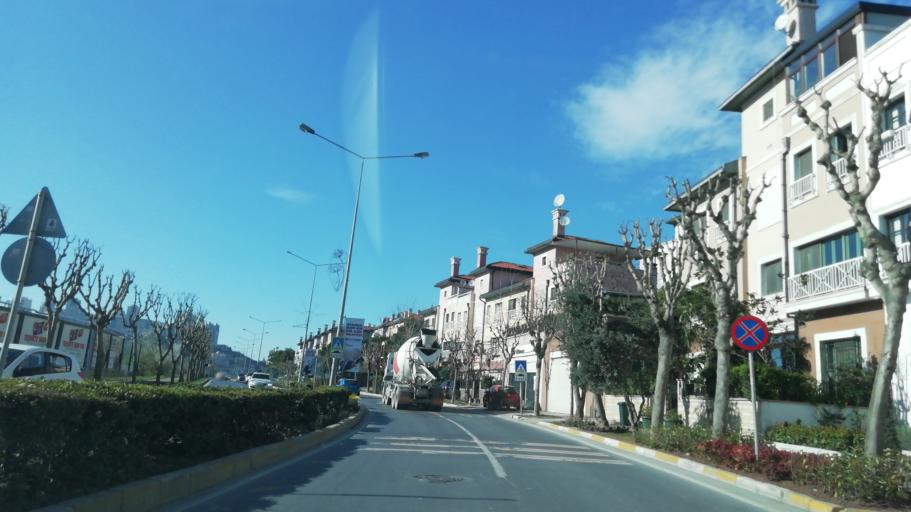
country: TR
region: Istanbul
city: Esenyurt
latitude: 41.0651
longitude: 28.6989
